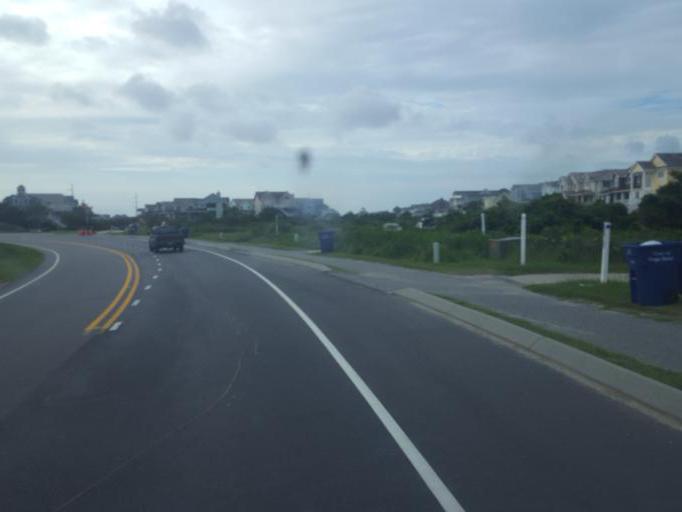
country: US
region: North Carolina
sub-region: Dare County
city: Nags Head
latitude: 35.9235
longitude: -75.6052
